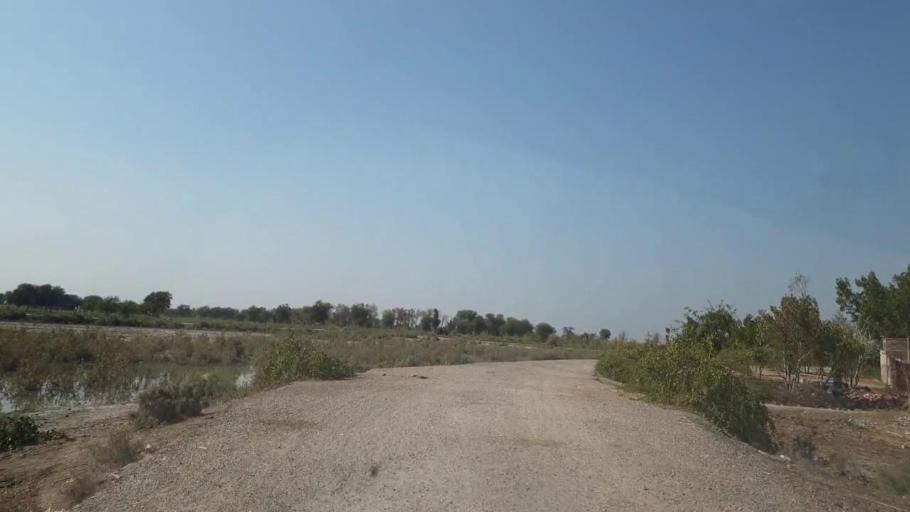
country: PK
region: Sindh
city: Mirpur Khas
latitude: 25.7161
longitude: 69.1310
